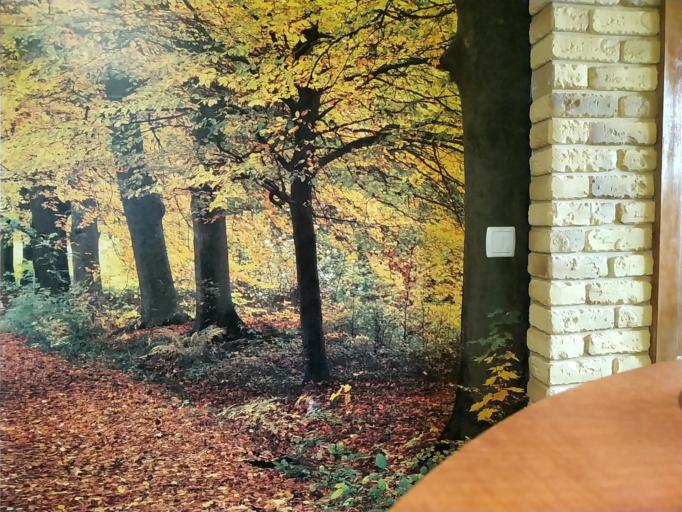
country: RU
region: Novgorod
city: Opechenskiy Posad
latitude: 58.2693
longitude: 34.0156
